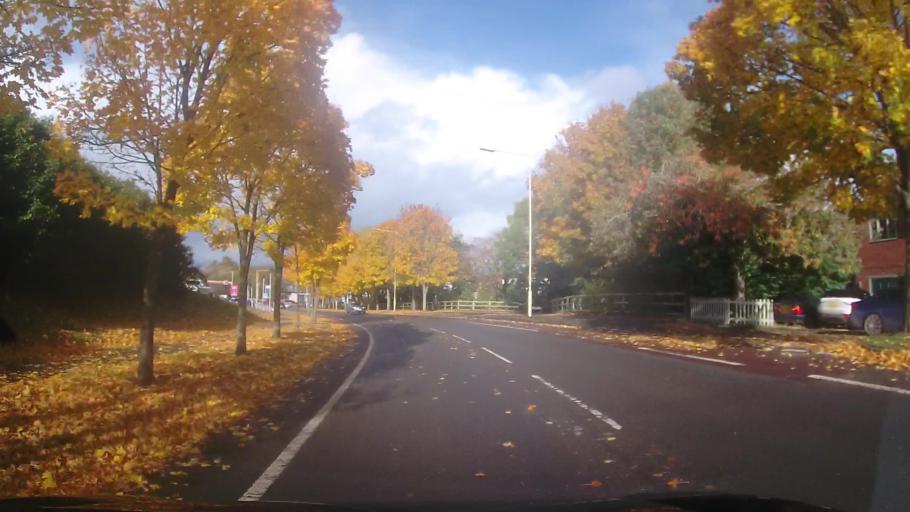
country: GB
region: England
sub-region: Shropshire
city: Whitchurch
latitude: 52.9653
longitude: -2.6790
